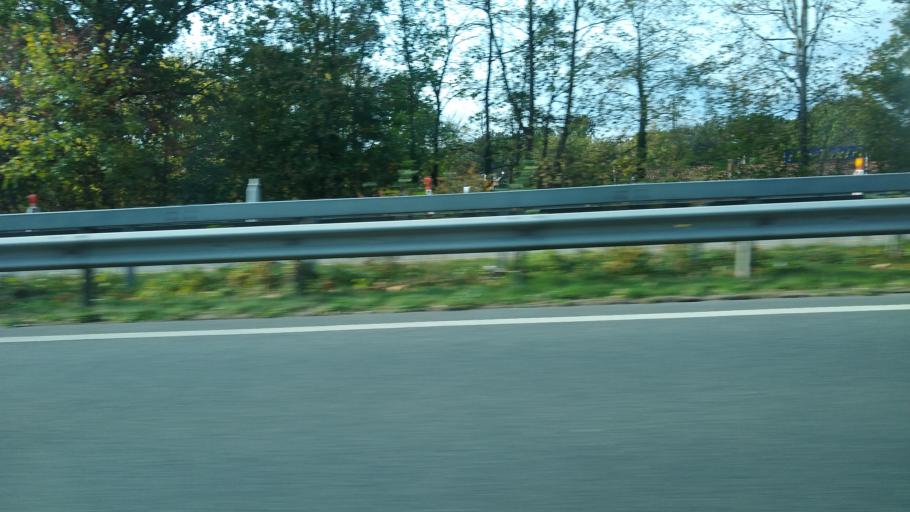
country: DE
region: Lower Saxony
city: Oldenburg
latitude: 53.1773
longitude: 8.2258
